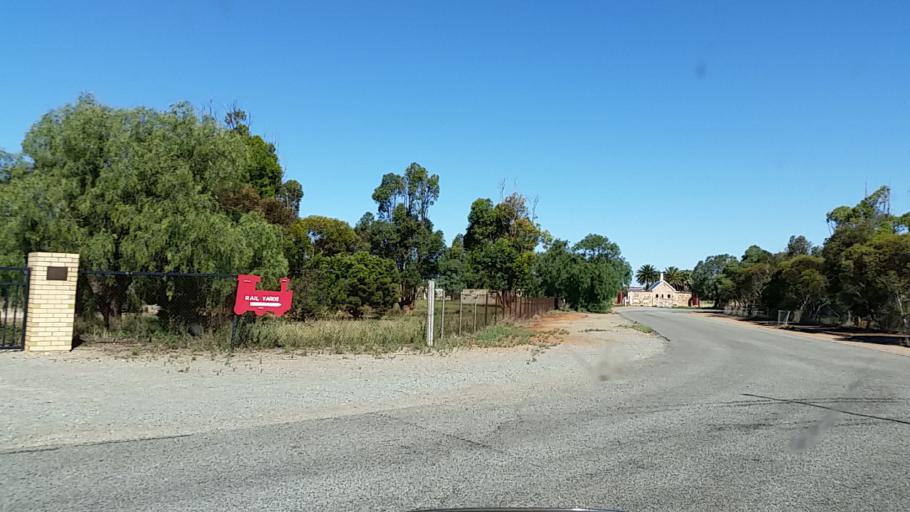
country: AU
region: South Australia
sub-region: Peterborough
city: Peterborough
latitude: -33.1494
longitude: 138.9201
